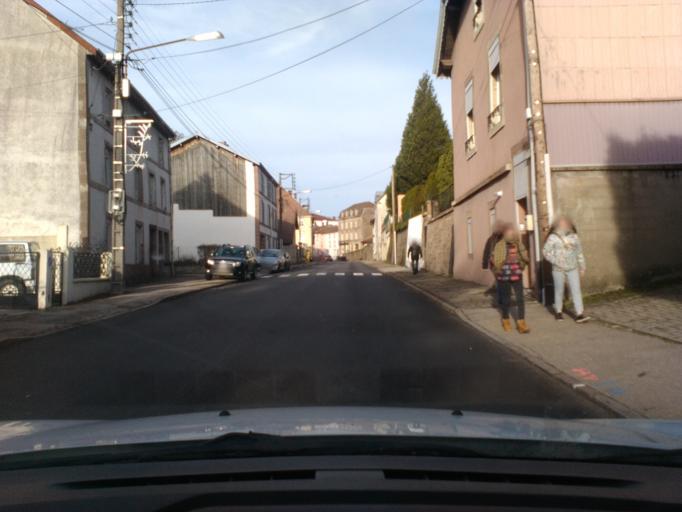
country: FR
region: Lorraine
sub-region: Departement des Vosges
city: Bruyeres
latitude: 48.2066
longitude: 6.7219
